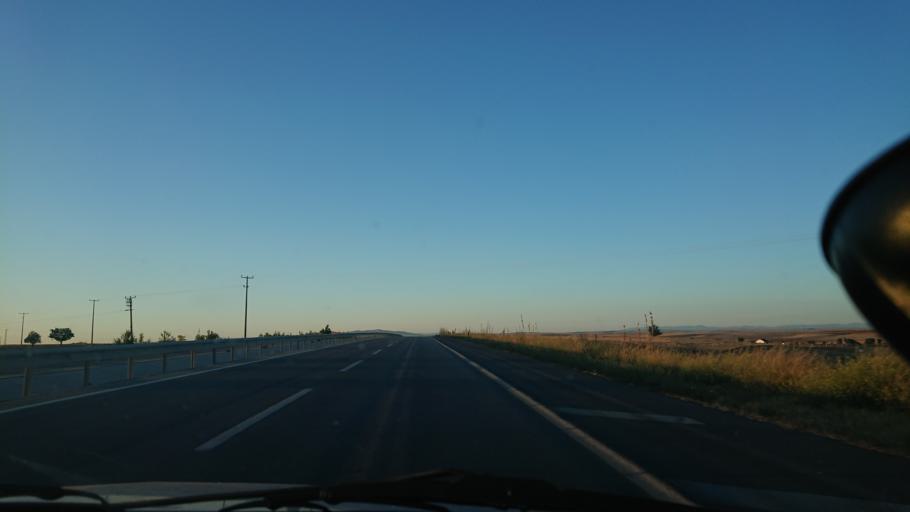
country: TR
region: Eskisehir
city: Mahmudiye
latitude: 39.5064
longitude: 30.9656
